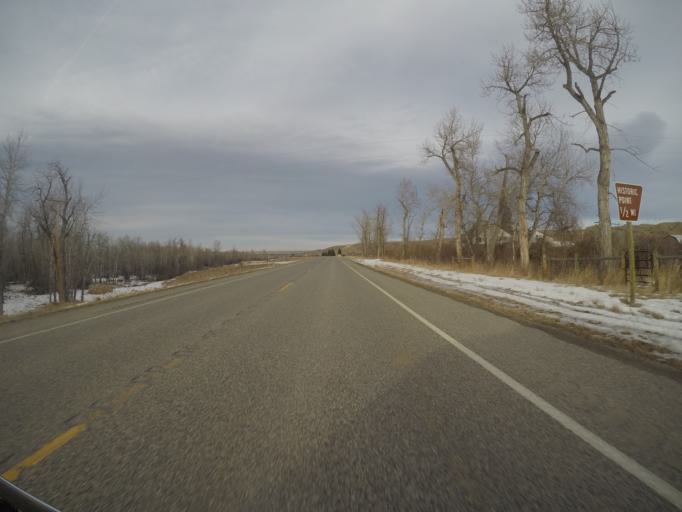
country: US
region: Montana
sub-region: Stillwater County
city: Absarokee
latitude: 45.4662
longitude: -109.4478
